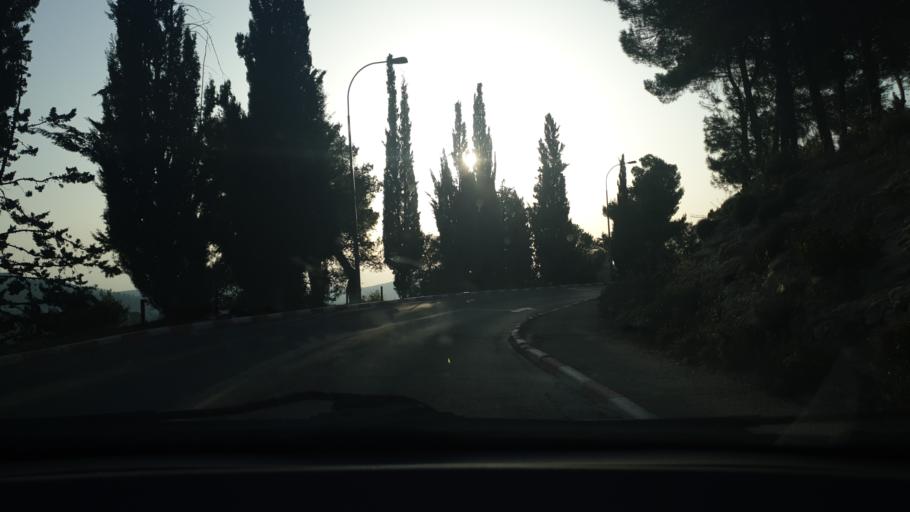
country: IL
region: Jerusalem
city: Jerusalem
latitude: 31.7719
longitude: 35.1789
